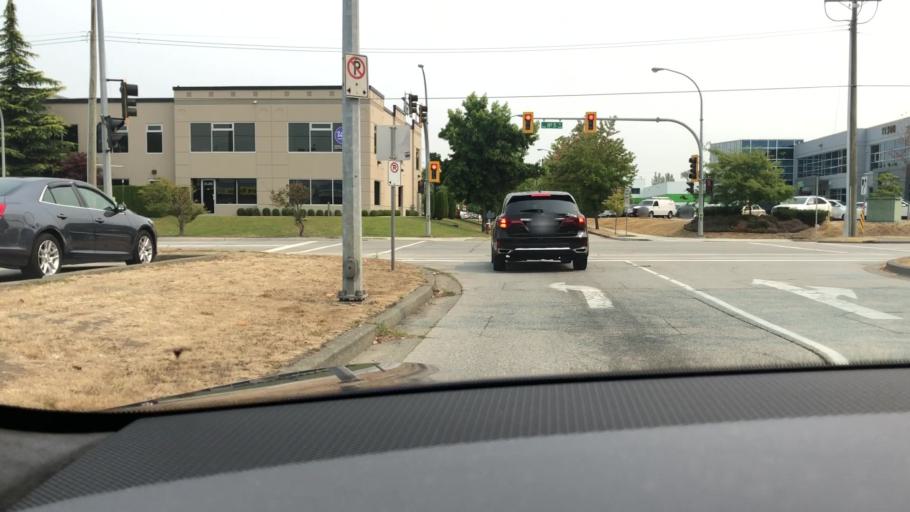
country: CA
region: British Columbia
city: Ladner
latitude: 49.1304
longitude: -123.0926
